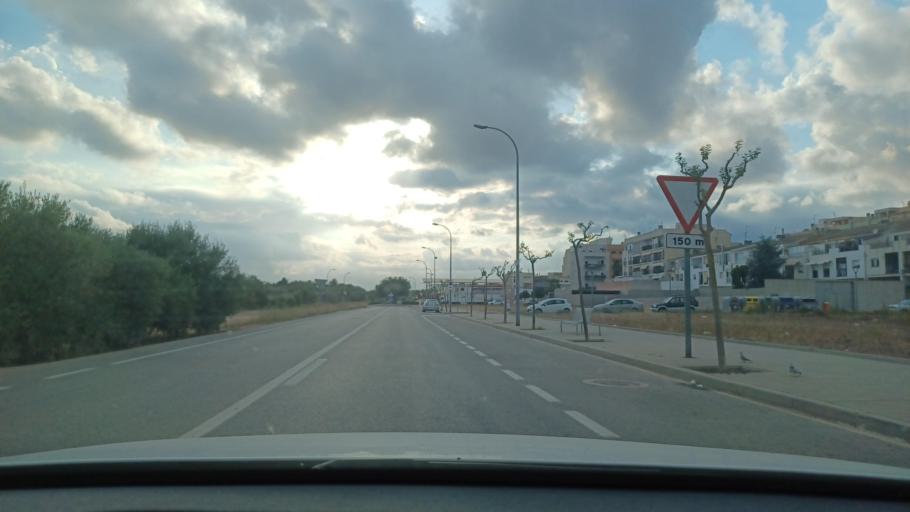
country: ES
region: Catalonia
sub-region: Provincia de Tarragona
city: Alcanar
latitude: 40.5394
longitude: 0.4805
